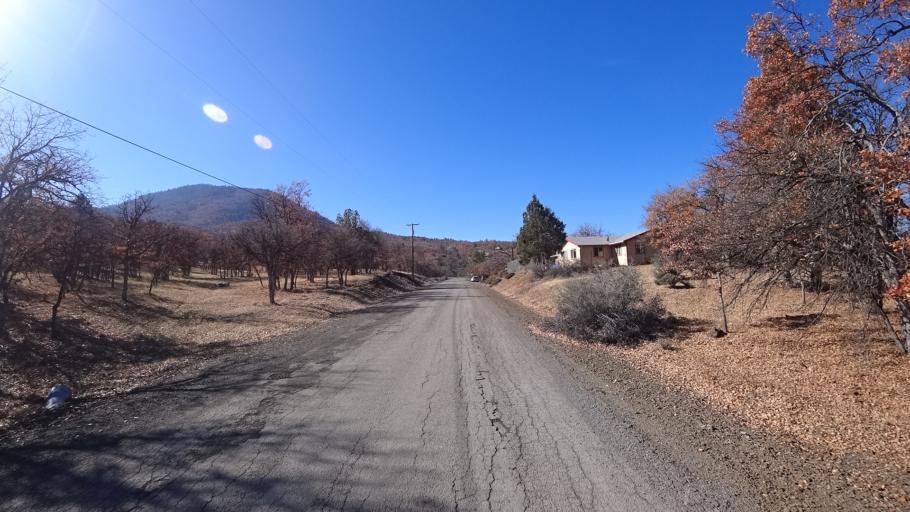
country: US
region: California
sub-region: Siskiyou County
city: Montague
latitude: 41.8842
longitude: -122.4891
